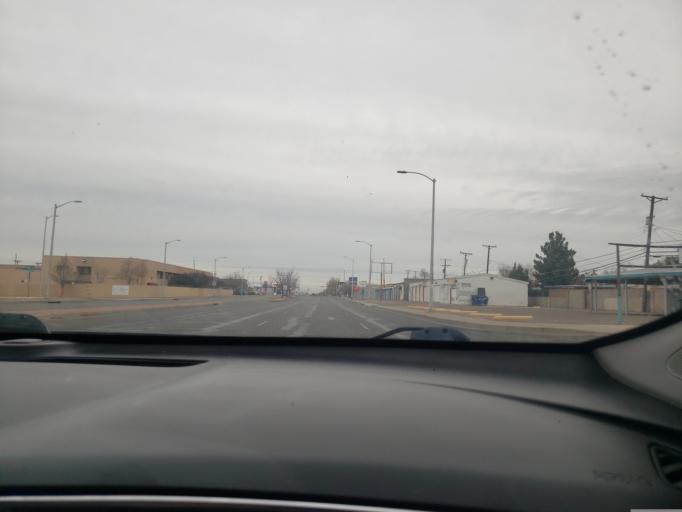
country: US
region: New Mexico
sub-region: Bernalillo County
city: Albuquerque
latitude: 35.0848
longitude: -106.5861
